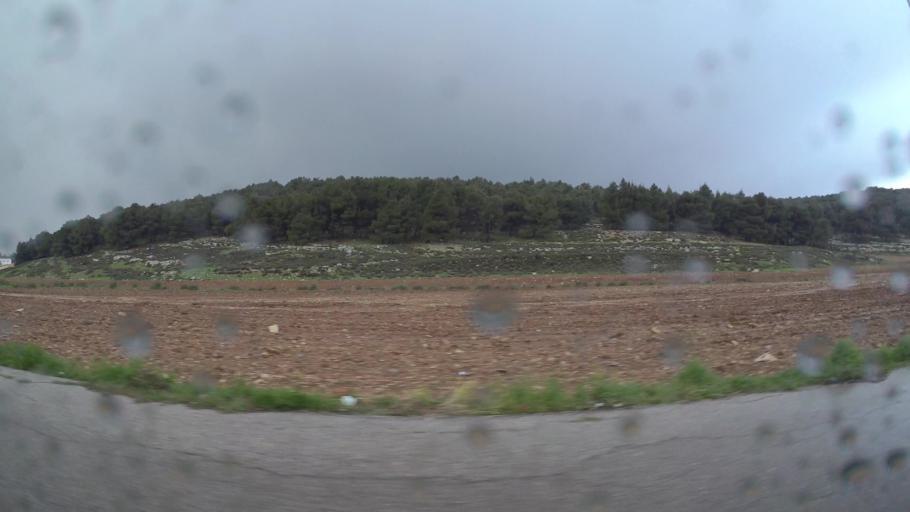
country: JO
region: Amman
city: Umm as Summaq
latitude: 31.8657
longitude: 35.8666
